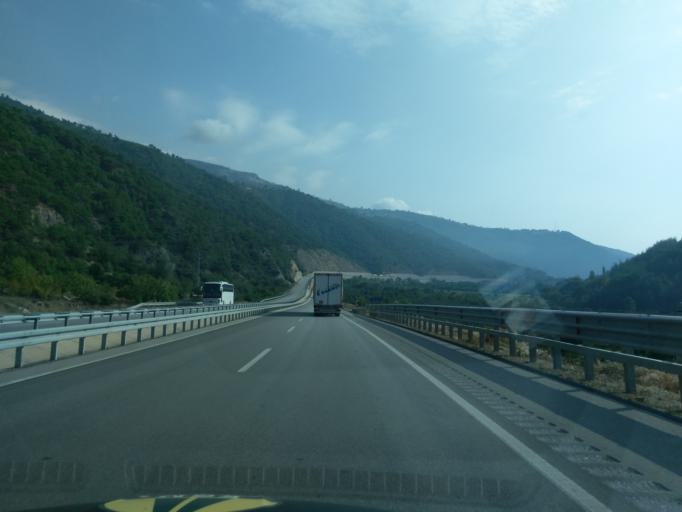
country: TR
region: Amasya
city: Akdag
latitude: 40.7503
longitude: 36.0577
